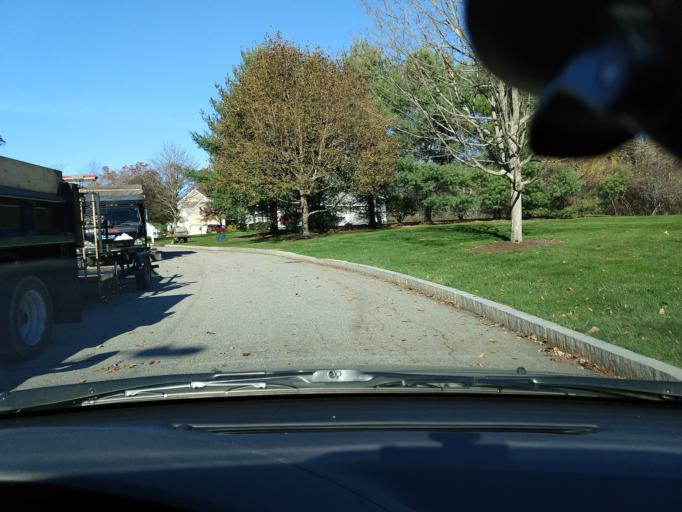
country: US
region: Massachusetts
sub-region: Middlesex County
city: Bedford
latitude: 42.5062
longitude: -71.2593
